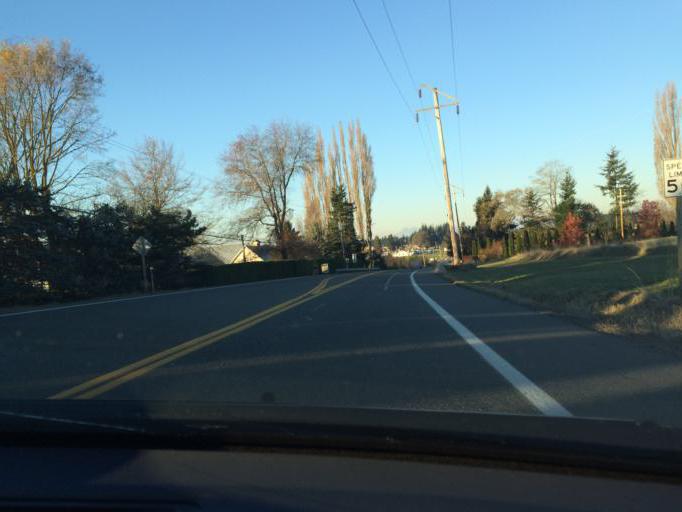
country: US
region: Washington
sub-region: Whatcom County
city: Lynden
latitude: 48.8556
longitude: -122.4427
